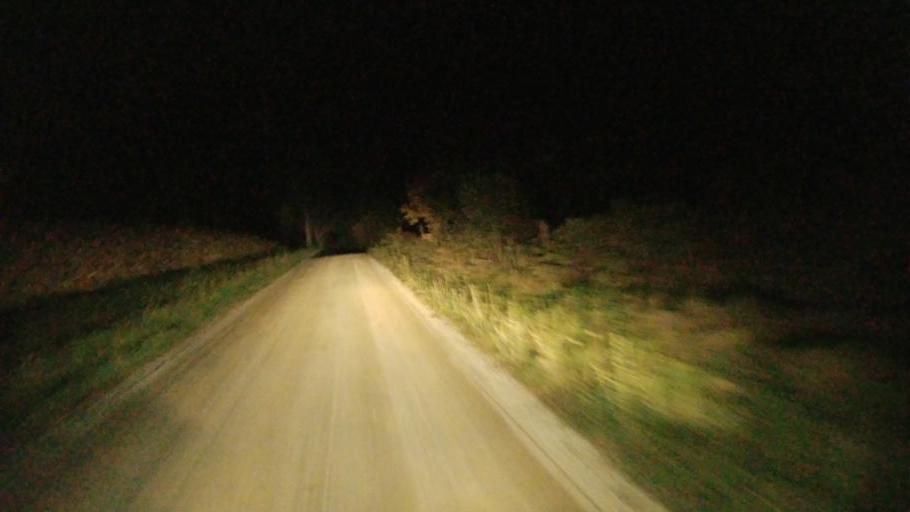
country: US
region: Ohio
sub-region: Richland County
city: Lexington
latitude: 40.6186
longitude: -82.6252
